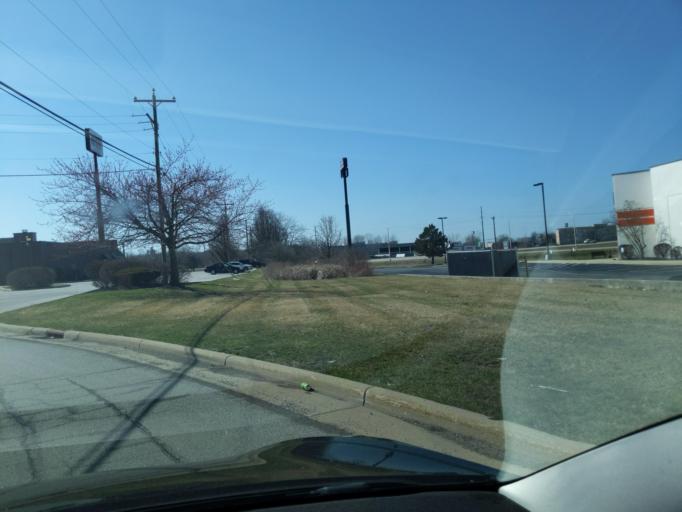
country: US
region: Ohio
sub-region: Allen County
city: Lima
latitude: 40.7274
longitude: -84.0731
